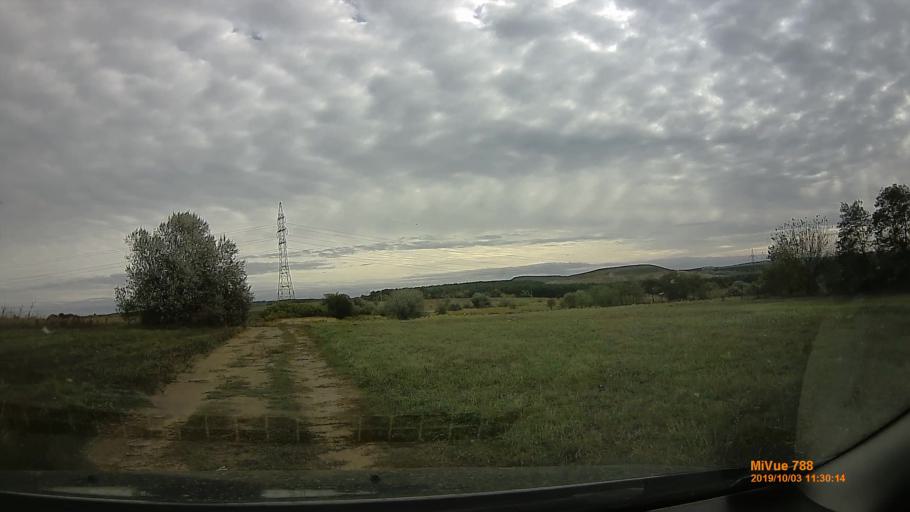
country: HU
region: Pest
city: Dunakeszi
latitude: 47.6547
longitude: 19.1620
